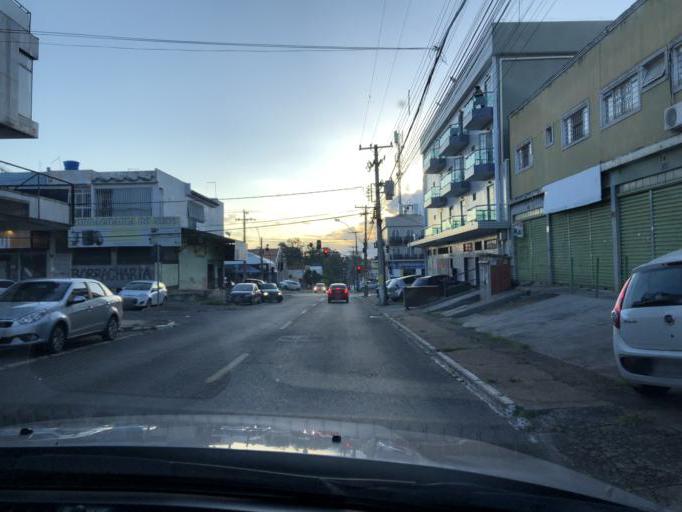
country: BR
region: Federal District
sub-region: Brasilia
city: Brasilia
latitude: -15.8473
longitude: -48.0478
